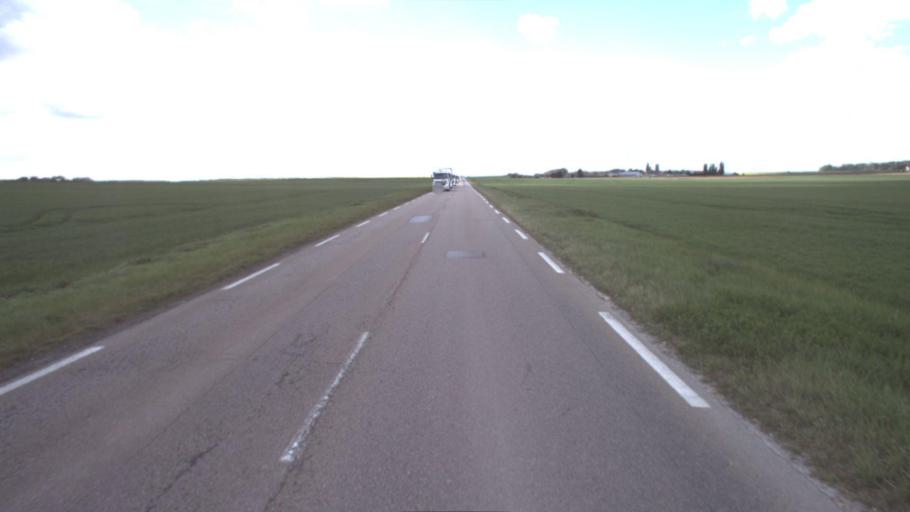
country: FR
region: Ile-de-France
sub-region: Departement de Seine-et-Marne
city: Villiers-Saint-Georges
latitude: 48.6914
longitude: 3.3569
